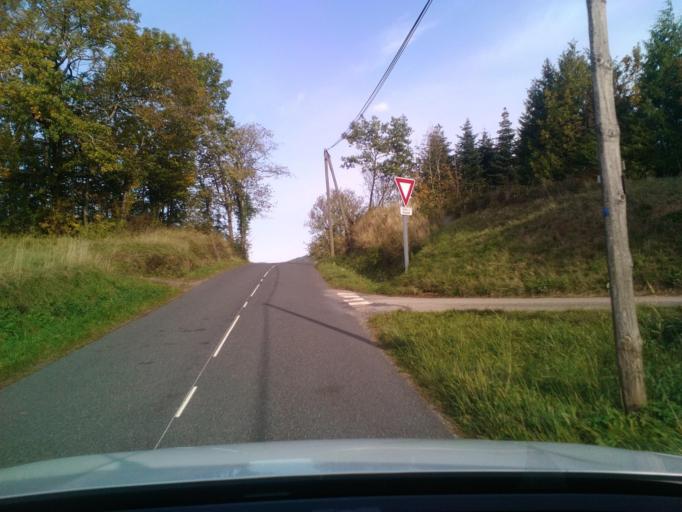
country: FR
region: Lorraine
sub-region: Departement des Vosges
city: Senones
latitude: 48.3481
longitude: 7.0204
